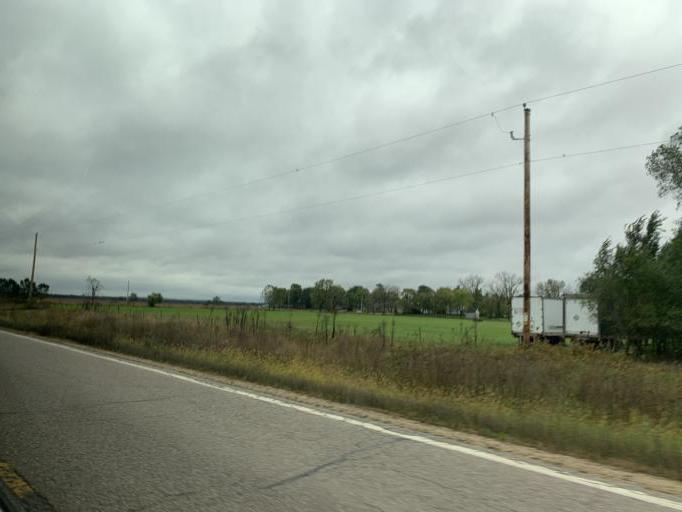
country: US
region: Wisconsin
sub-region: Sauk County
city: Spring Green
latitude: 43.1898
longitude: -90.0665
